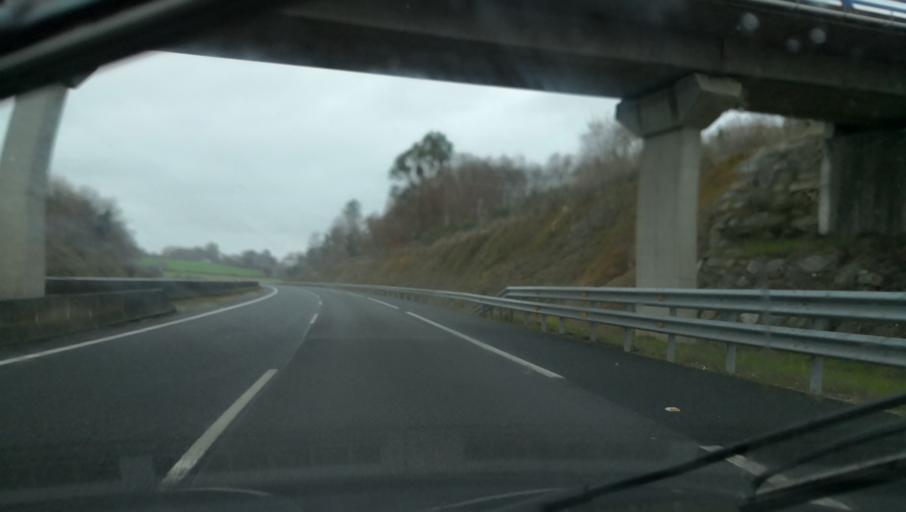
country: ES
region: Galicia
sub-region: Provincia de Pontevedra
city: Lalin
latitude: 42.6831
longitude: -8.1632
